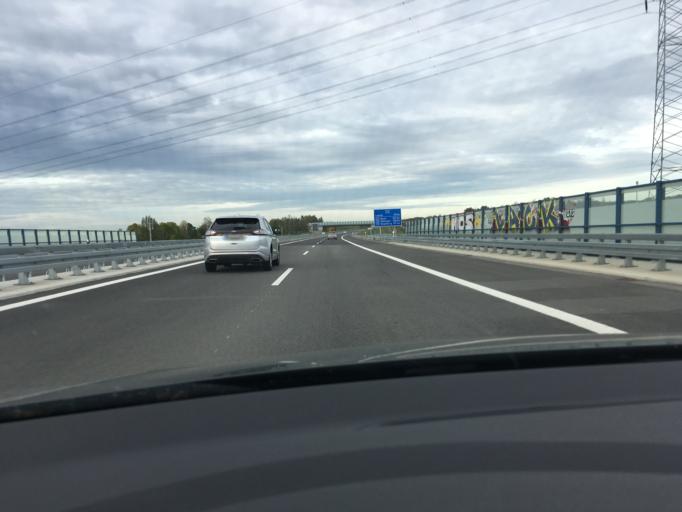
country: DE
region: Saxony
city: Borna
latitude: 51.1480
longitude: 12.5032
